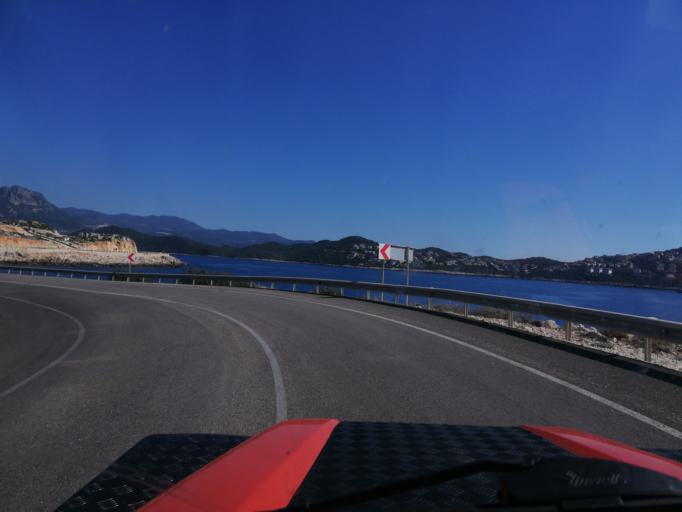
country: GR
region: South Aegean
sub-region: Nomos Dodekanisou
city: Megisti
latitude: 36.2020
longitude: 29.5799
